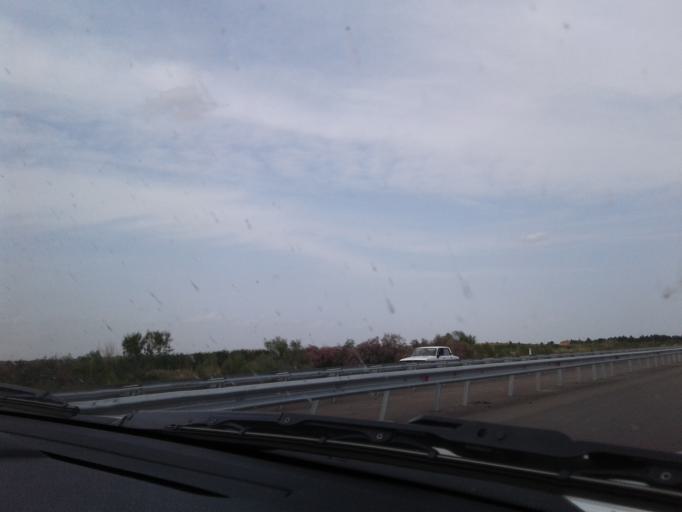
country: TM
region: Mary
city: Mary
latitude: 37.4242
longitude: 61.5871
